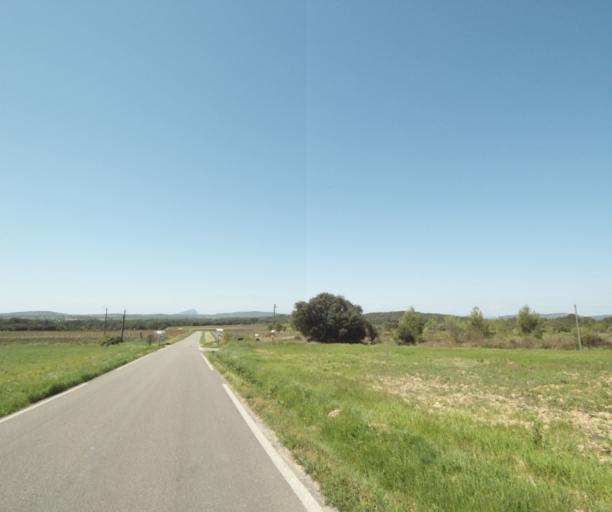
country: FR
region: Languedoc-Roussillon
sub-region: Departement de l'Herault
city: Beaulieu
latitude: 43.7314
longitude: 4.0155
